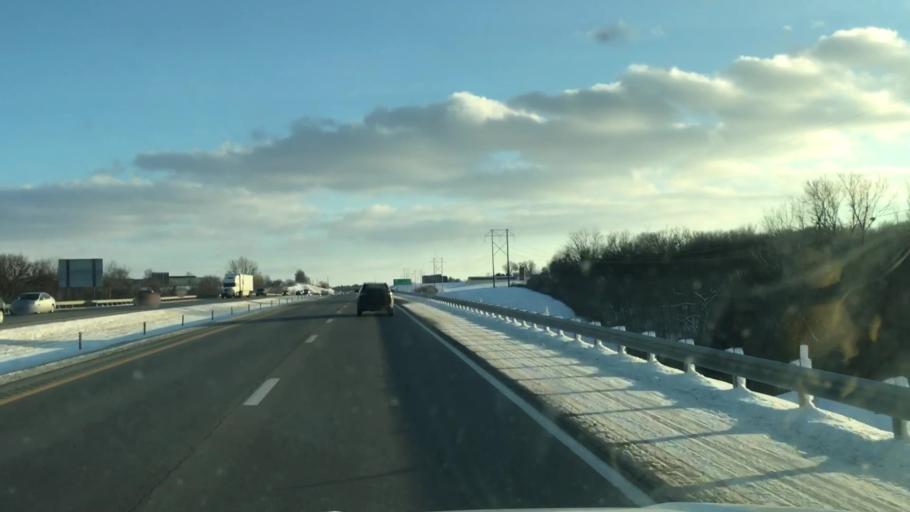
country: US
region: Missouri
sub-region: Buchanan County
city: Saint Joseph
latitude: 39.7656
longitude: -94.7921
